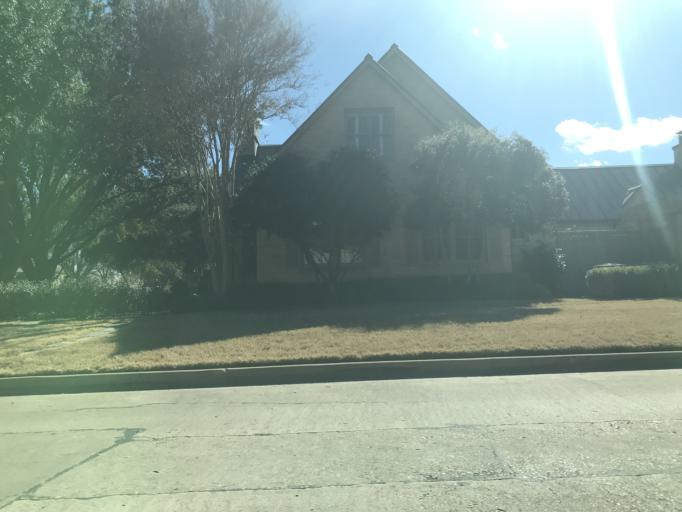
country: US
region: Texas
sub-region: Tom Green County
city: San Angelo
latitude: 31.4474
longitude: -100.4512
